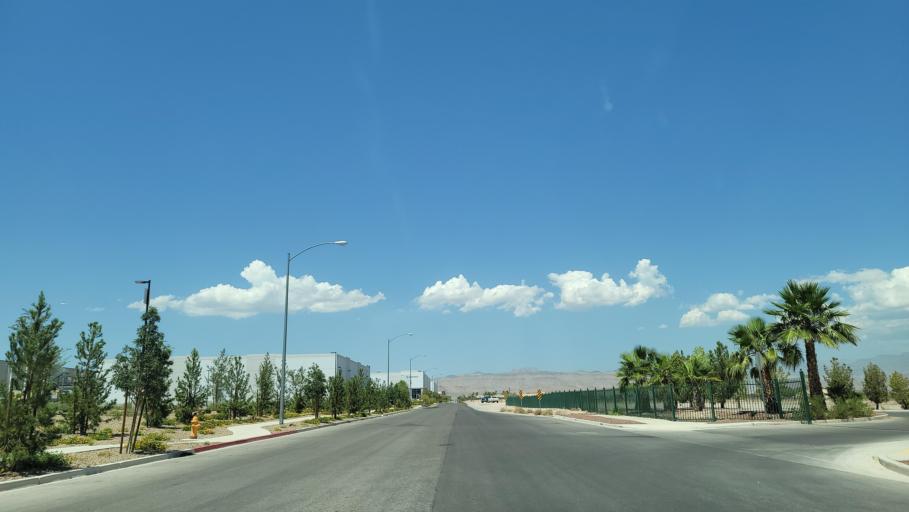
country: US
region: Nevada
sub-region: Clark County
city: Spring Valley
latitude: 36.0745
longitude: -115.2295
